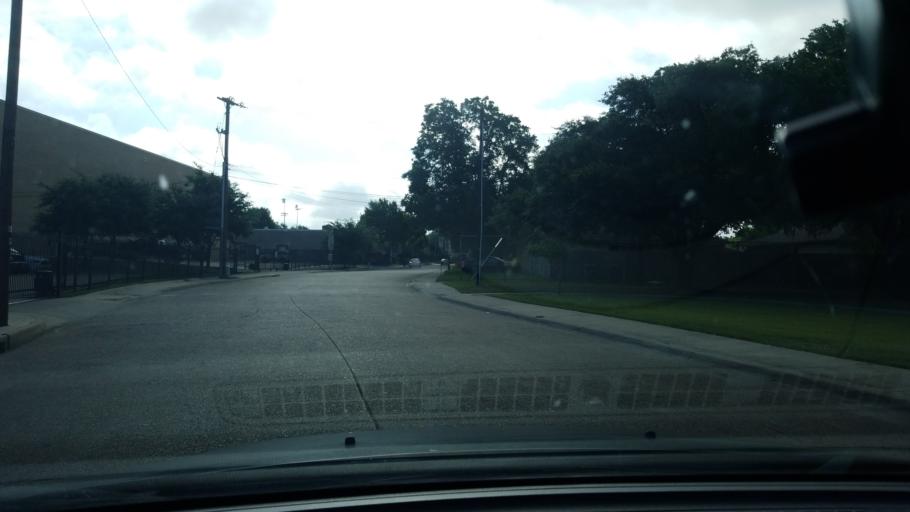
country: US
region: Texas
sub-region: Dallas County
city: Mesquite
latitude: 32.8179
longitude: -96.6817
